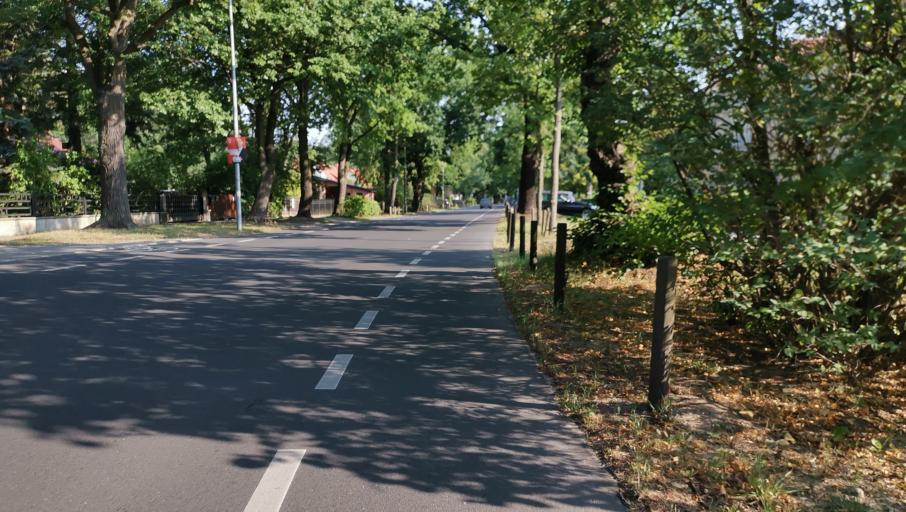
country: DE
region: Brandenburg
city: Potsdam
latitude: 52.3890
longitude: 13.0116
